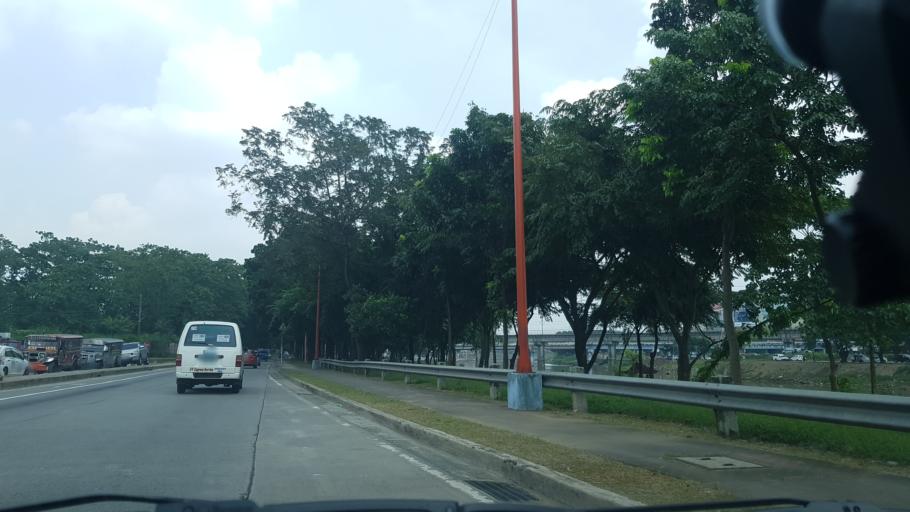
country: PH
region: Metro Manila
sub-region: Marikina
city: Calumpang
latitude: 14.6232
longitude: 121.0813
